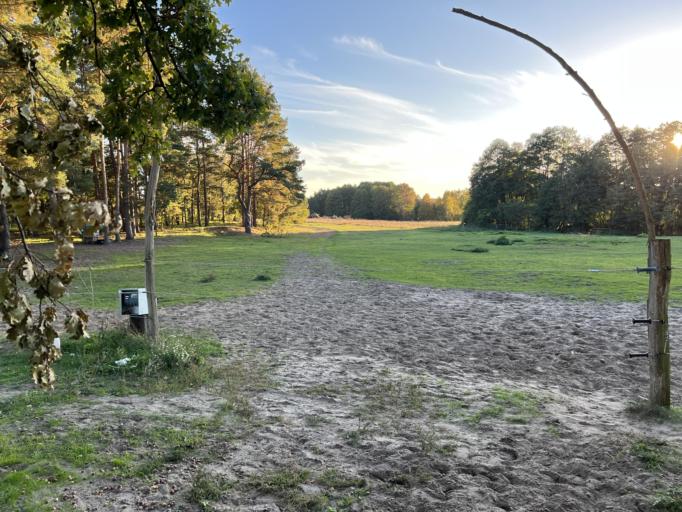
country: DE
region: Brandenburg
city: Teupitz
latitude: 52.1262
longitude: 13.5854
